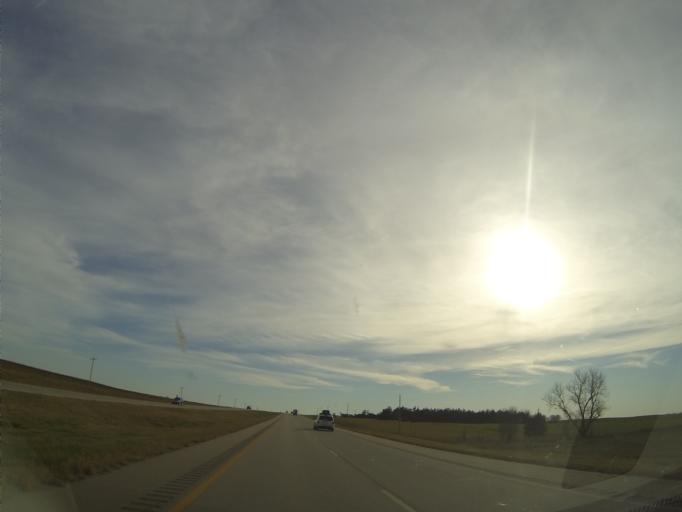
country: US
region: Kansas
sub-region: Ottawa County
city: Minneapolis
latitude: 39.1743
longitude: -97.6683
